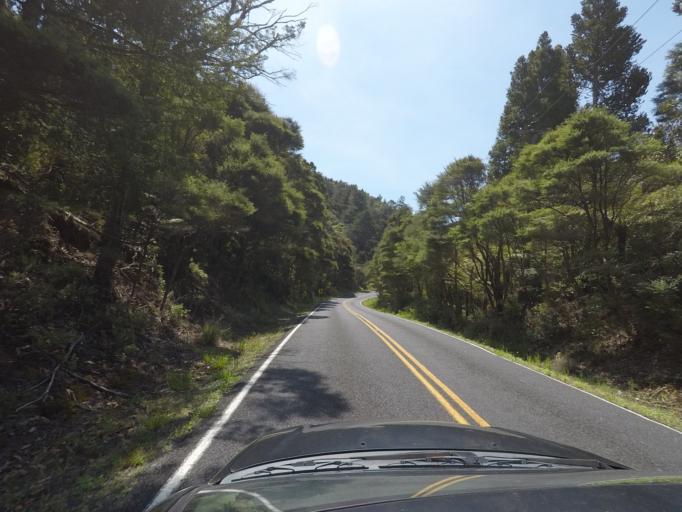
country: NZ
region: Auckland
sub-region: Auckland
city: Titirangi
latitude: -36.9811
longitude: 174.6056
